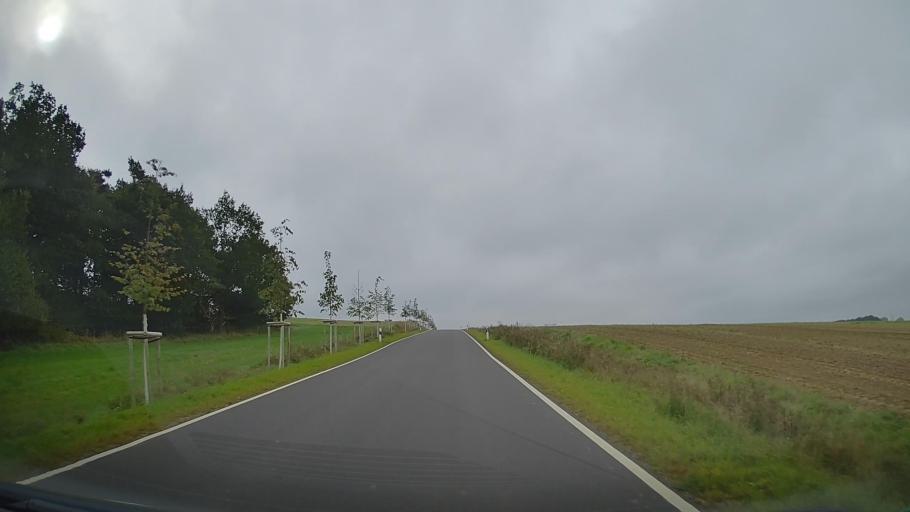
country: DE
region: Mecklenburg-Vorpommern
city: Kavelstorf
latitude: 53.9348
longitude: 12.2082
